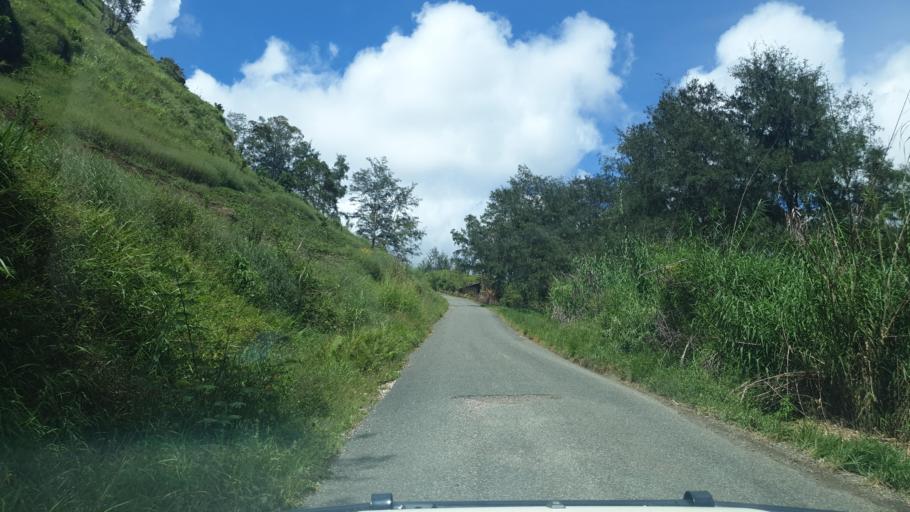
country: PG
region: Chimbu
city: Kundiawa
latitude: -6.1519
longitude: 145.1334
